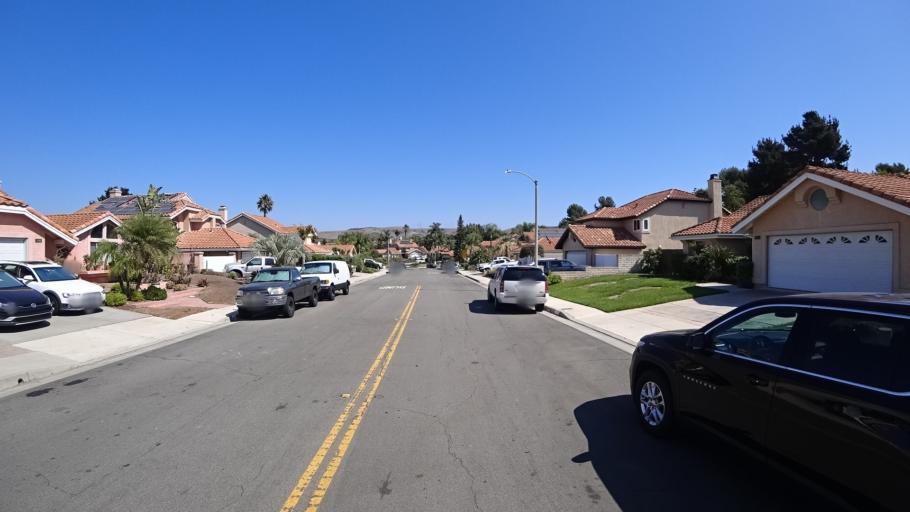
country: US
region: California
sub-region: Orange County
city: San Clemente
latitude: 33.4666
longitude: -117.6280
